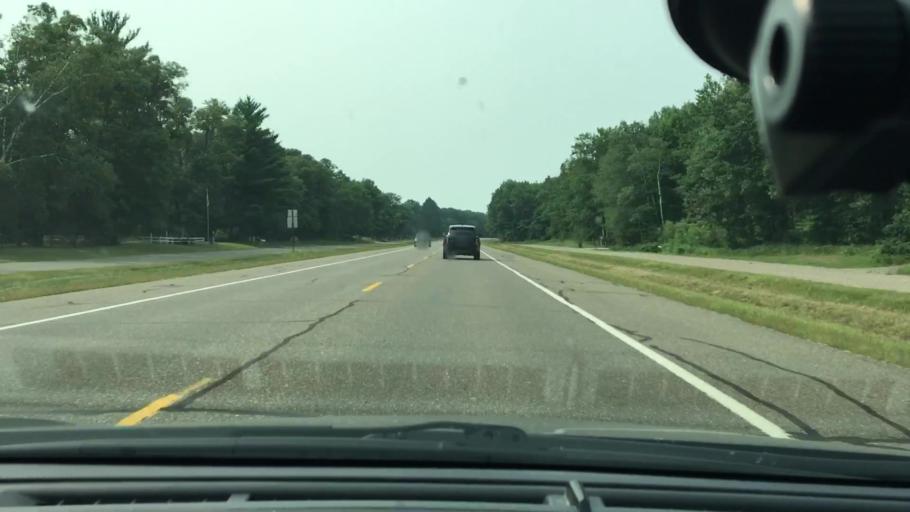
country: US
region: Minnesota
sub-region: Crow Wing County
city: Breezy Point
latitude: 46.4985
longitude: -94.1449
